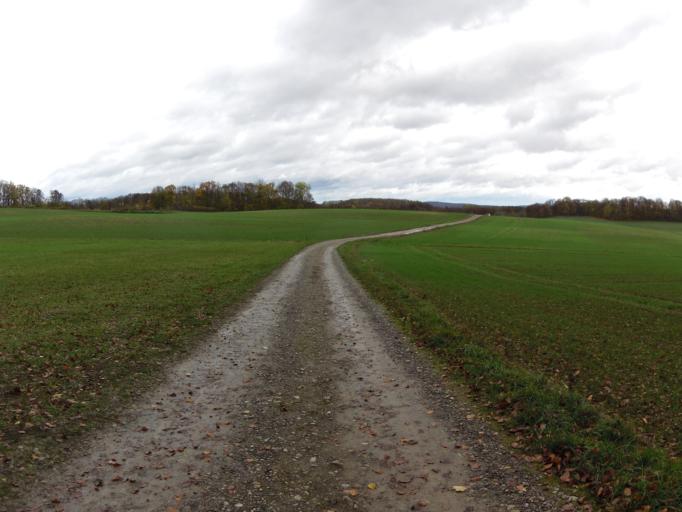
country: DE
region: Hesse
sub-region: Regierungsbezirk Kassel
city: Herleshausen
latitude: 51.0425
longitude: 10.1278
